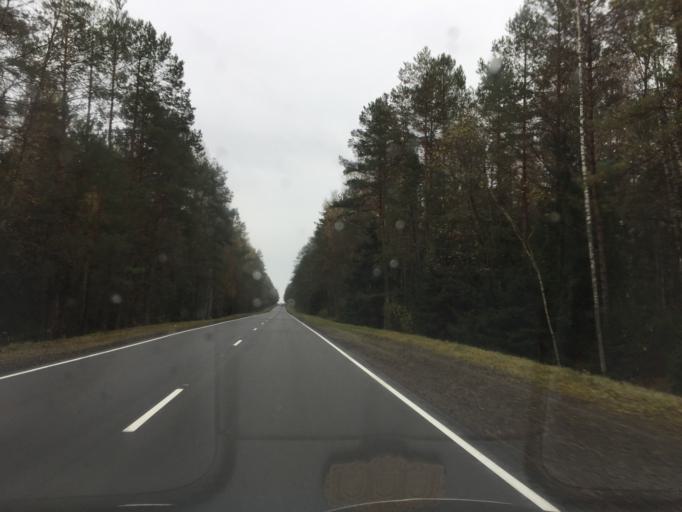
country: BY
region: Mogilev
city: Cherykaw
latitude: 53.6433
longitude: 31.2705
